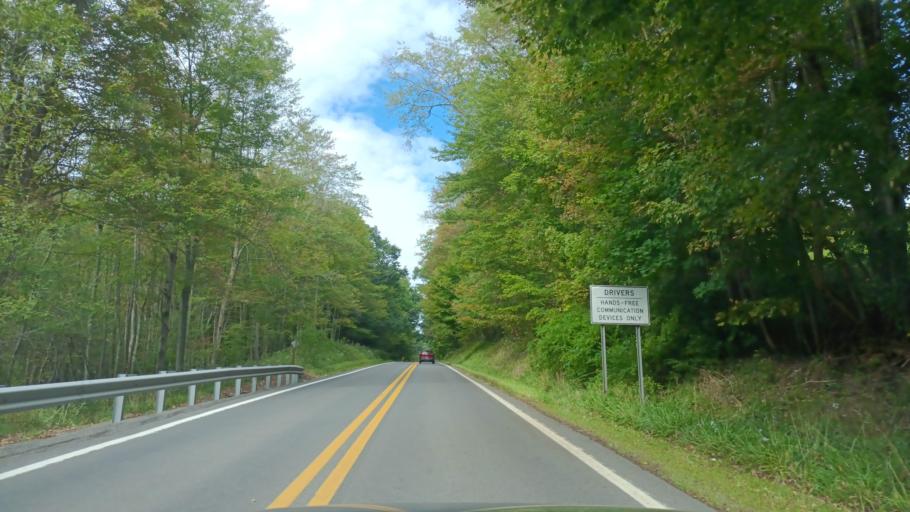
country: US
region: Maryland
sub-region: Garrett County
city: Oakland
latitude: 39.3193
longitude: -79.4906
